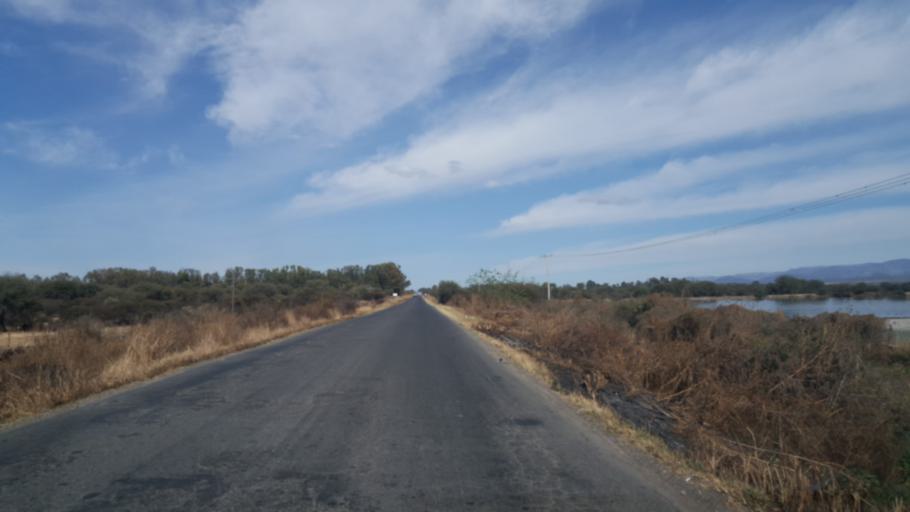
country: MX
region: Jalisco
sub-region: Lagos de Moreno
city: Cristeros [Fraccionamiento]
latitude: 21.2724
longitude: -101.9410
